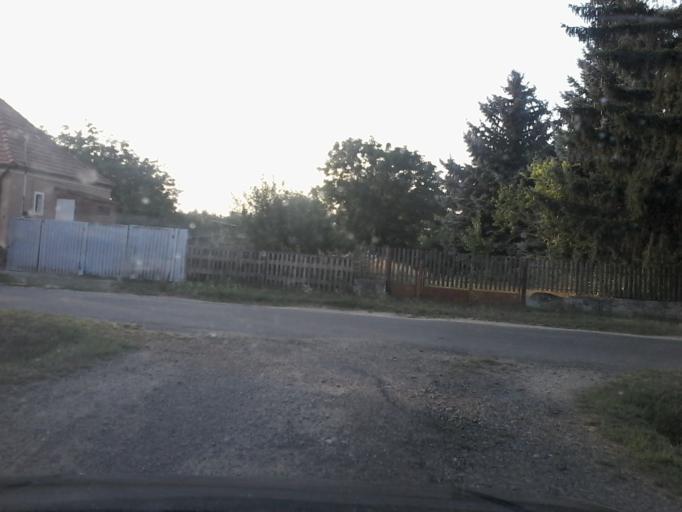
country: HU
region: Vas
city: Janoshaza
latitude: 47.0897
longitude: 17.1945
